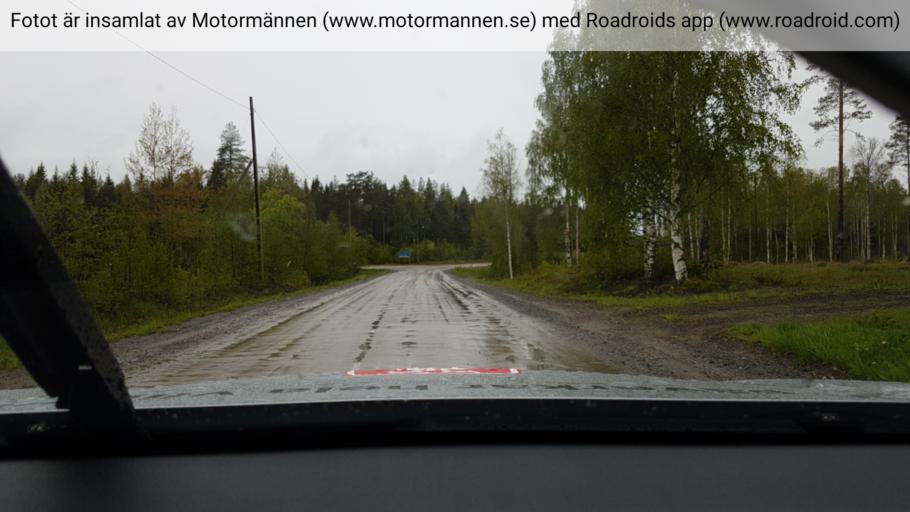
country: SE
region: Vaesterbotten
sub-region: Vannas Kommun
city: Vaennaes
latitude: 63.8558
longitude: 19.6238
